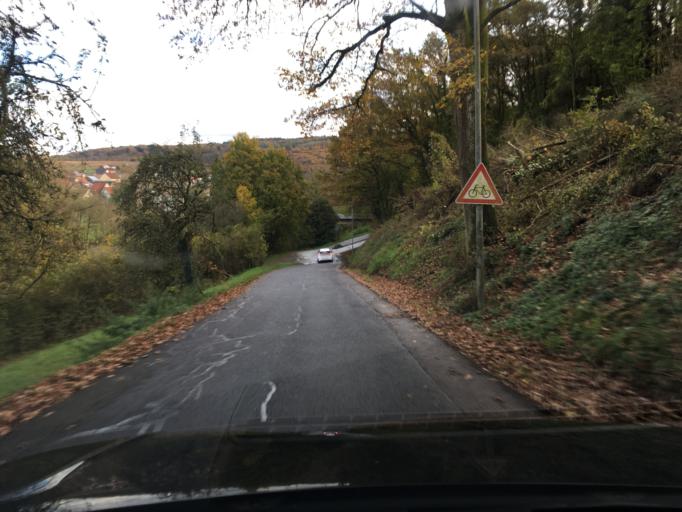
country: DE
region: Baden-Wuerttemberg
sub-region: Regierungsbezirk Stuttgart
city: Mockmuhl
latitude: 49.3200
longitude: 9.3741
